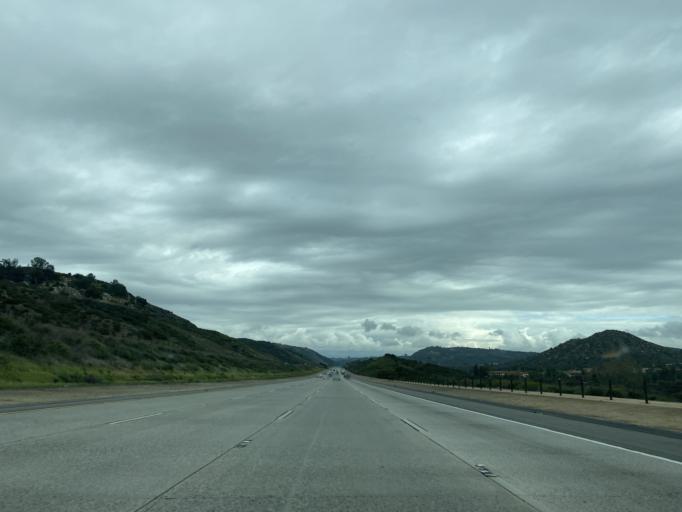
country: US
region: California
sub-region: San Diego County
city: Hidden Meadows
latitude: 33.2254
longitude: -117.1435
